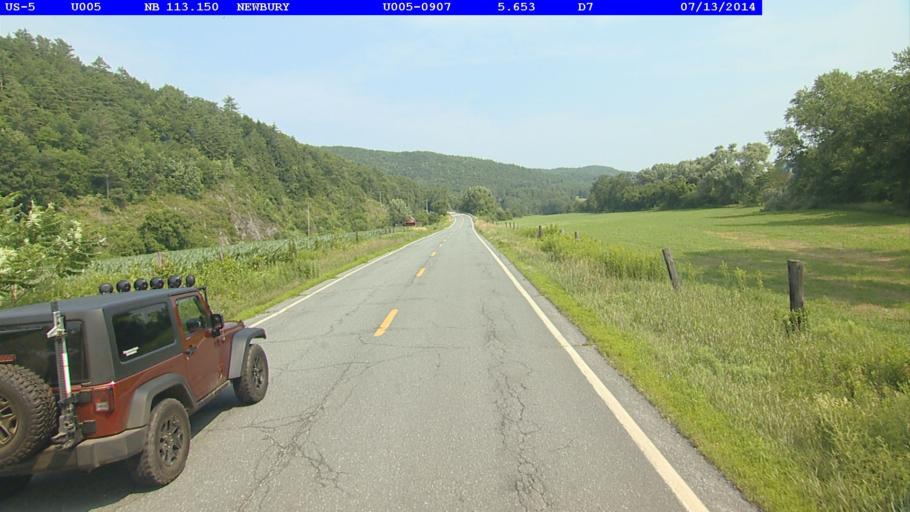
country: US
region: New Hampshire
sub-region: Grafton County
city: North Haverhill
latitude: 44.1022
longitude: -72.0533
